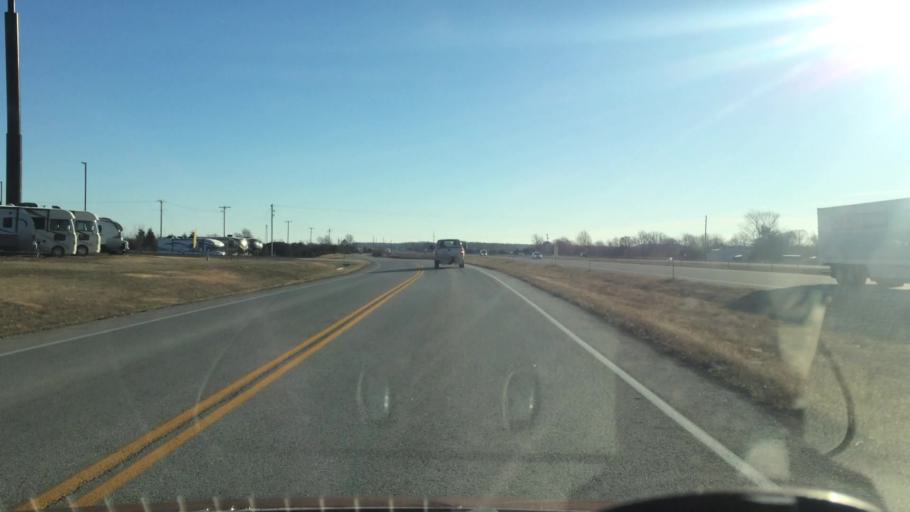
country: US
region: Missouri
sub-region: Greene County
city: Strafford
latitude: 37.2719
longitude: -93.1067
